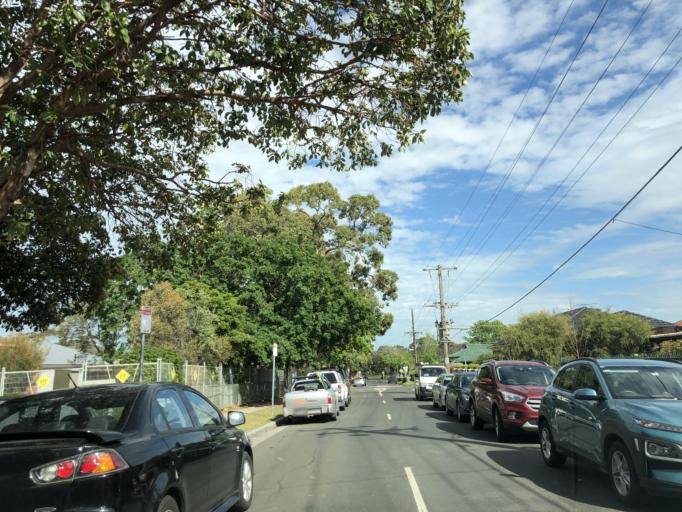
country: AU
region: Victoria
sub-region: Greater Dandenong
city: Dandenong
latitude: -37.9806
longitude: 145.2007
